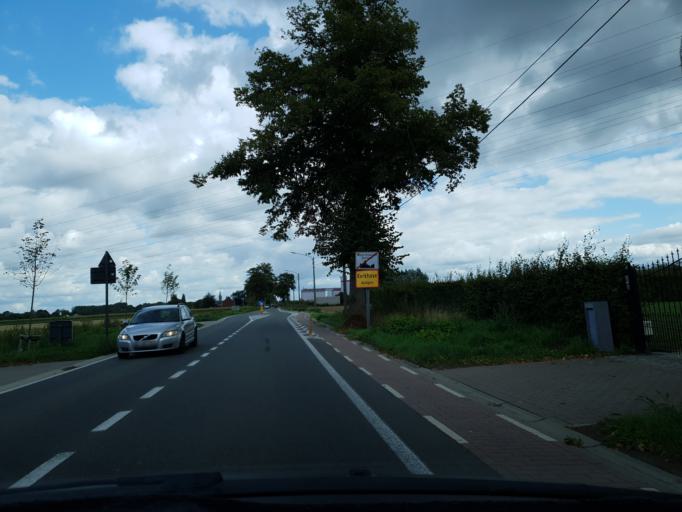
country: BE
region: Flanders
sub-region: Provincie West-Vlaanderen
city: Anzegem
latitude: 50.7923
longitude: 3.4890
